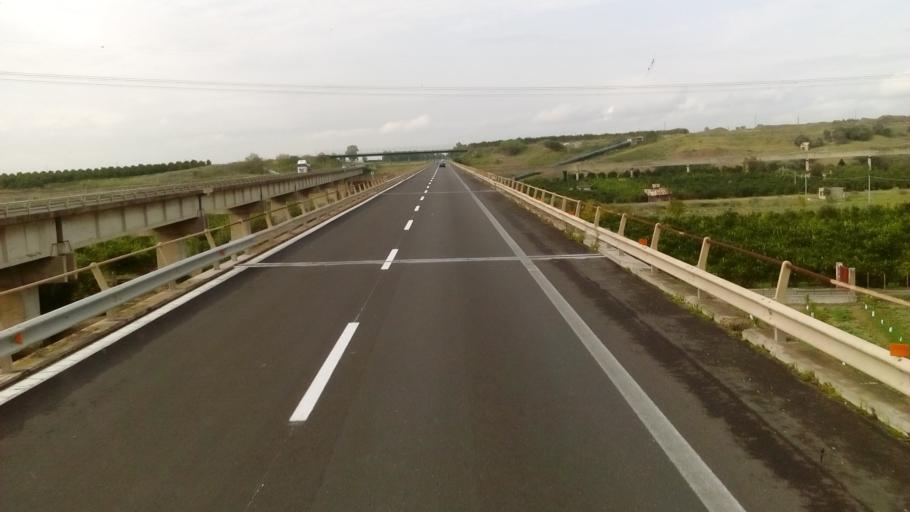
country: IT
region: Sicily
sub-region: Catania
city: Motta Sant'Anastasia
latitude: 37.4683
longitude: 14.8800
